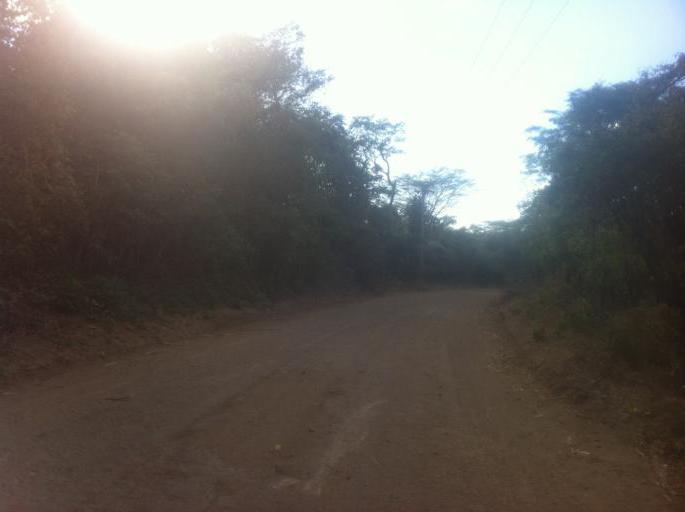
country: NI
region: Managua
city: Masachapa
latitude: 11.8296
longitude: -86.5055
